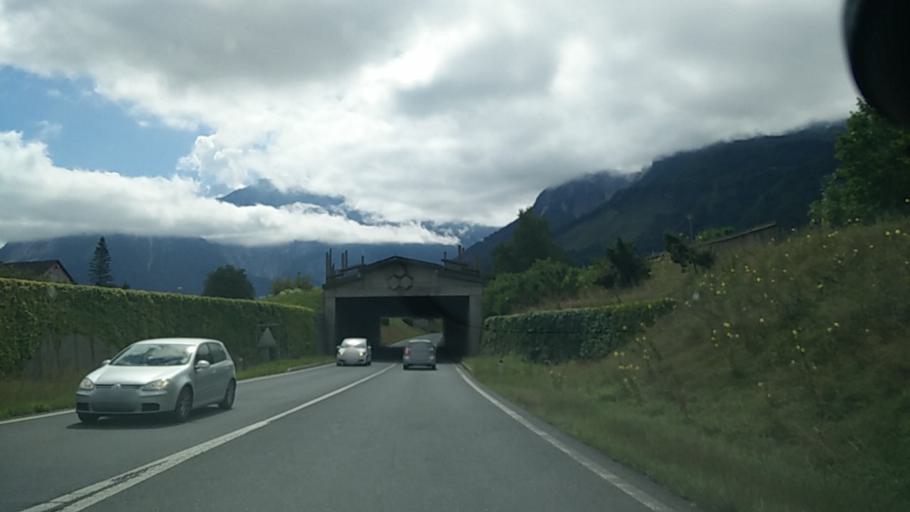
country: AT
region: Carinthia
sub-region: Politischer Bezirk Klagenfurt Land
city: Maria Rain
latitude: 46.5364
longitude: 14.2659
